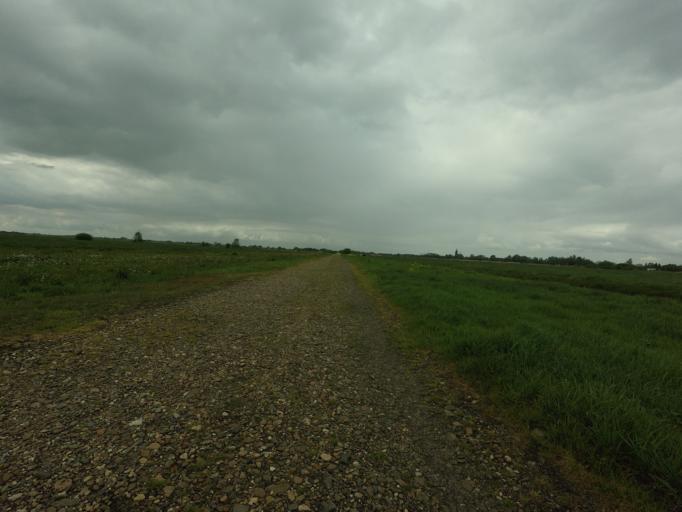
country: NL
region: Utrecht
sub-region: Stichtse Vecht
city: Breukelen
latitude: 52.2110
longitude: 4.9549
